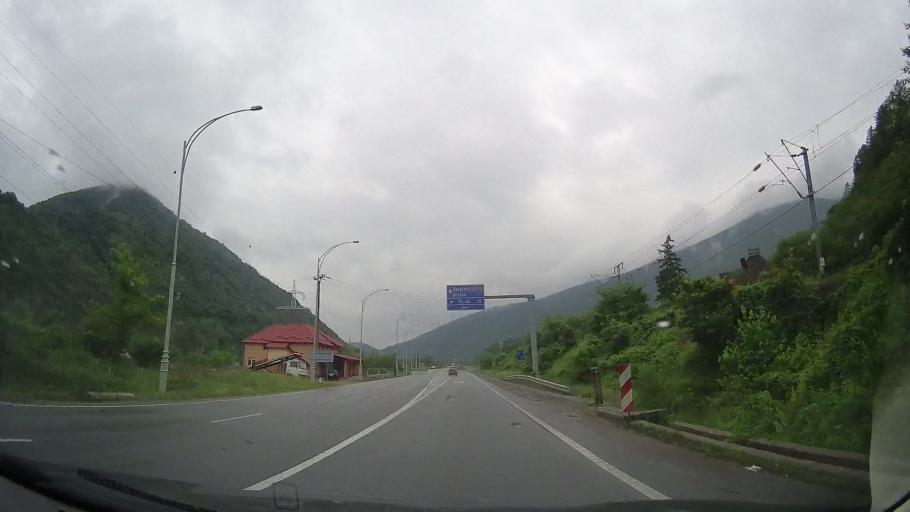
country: RO
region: Caras-Severin
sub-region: Oras Baile Herculane
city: Baile Herculane
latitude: 44.8587
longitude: 22.3882
